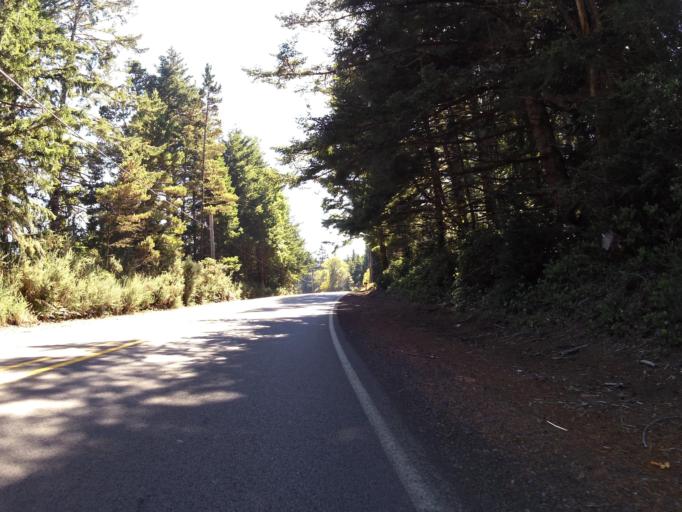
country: US
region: Oregon
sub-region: Coos County
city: Bandon
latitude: 43.2110
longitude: -124.3693
